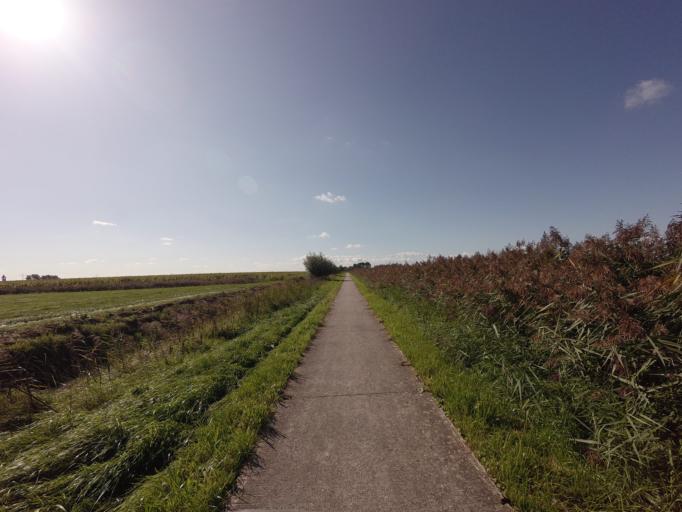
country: NL
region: Friesland
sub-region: Gemeente Boarnsterhim
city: Reduzum
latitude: 53.1333
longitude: 5.7574
